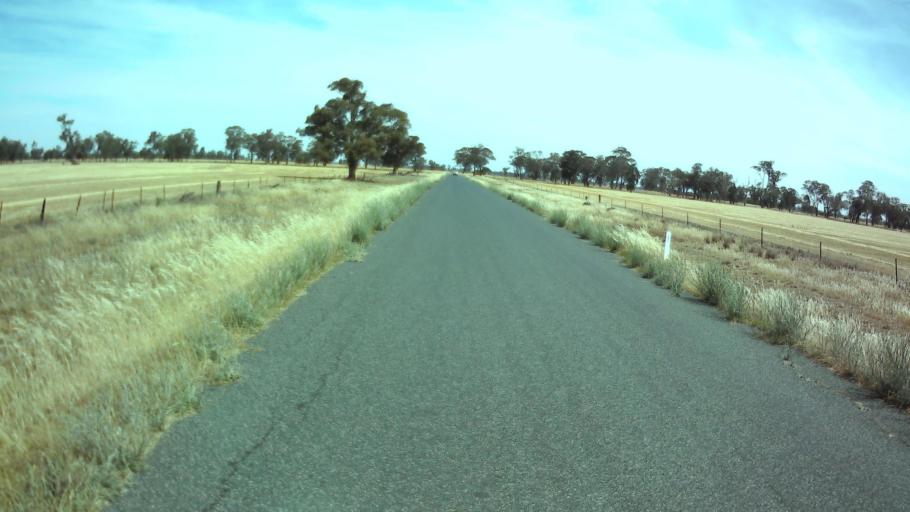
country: AU
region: New South Wales
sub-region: Weddin
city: Grenfell
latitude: -34.0019
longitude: 147.7739
